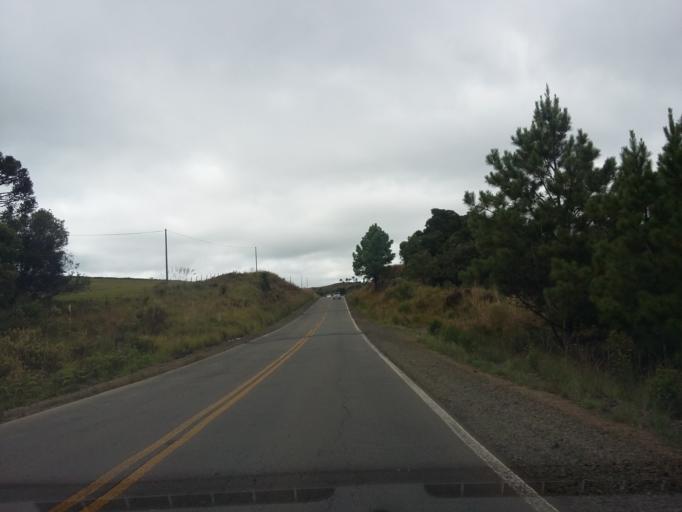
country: BR
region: Santa Catarina
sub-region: Lages
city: Lages
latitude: -27.8700
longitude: -50.1810
